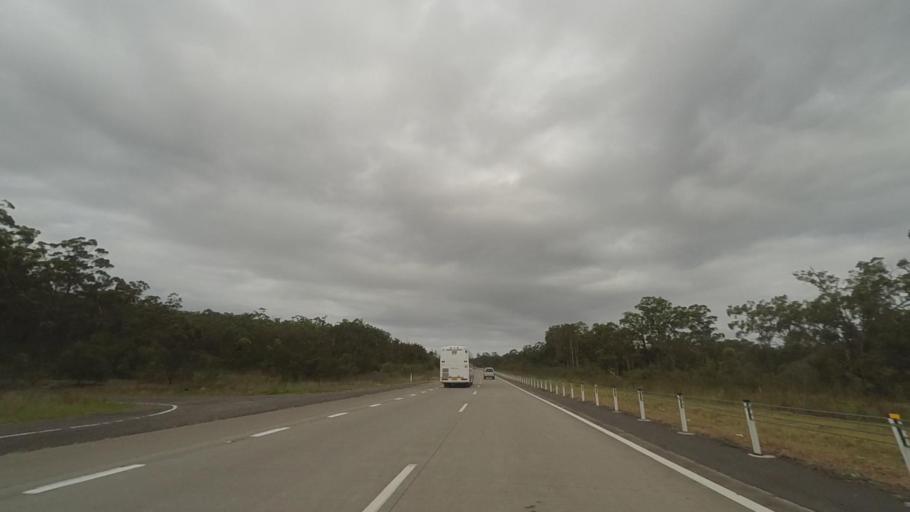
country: AU
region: New South Wales
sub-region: Port Stephens Shire
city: Port Stephens
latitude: -32.6222
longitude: 152.0649
